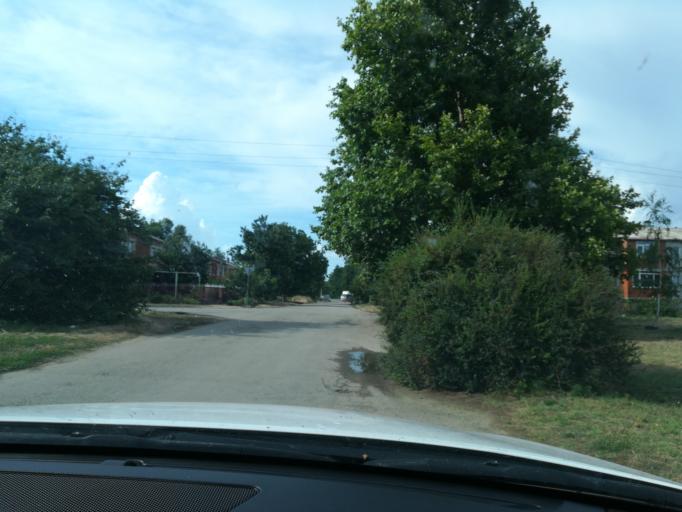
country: RU
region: Krasnodarskiy
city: Strelka
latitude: 45.1726
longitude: 37.2744
